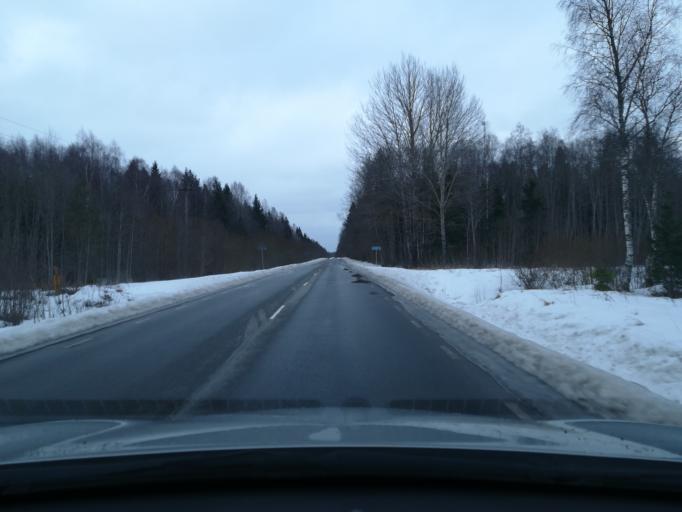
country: EE
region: Harju
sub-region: Nissi vald
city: Turba
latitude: 59.0712
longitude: 24.2491
